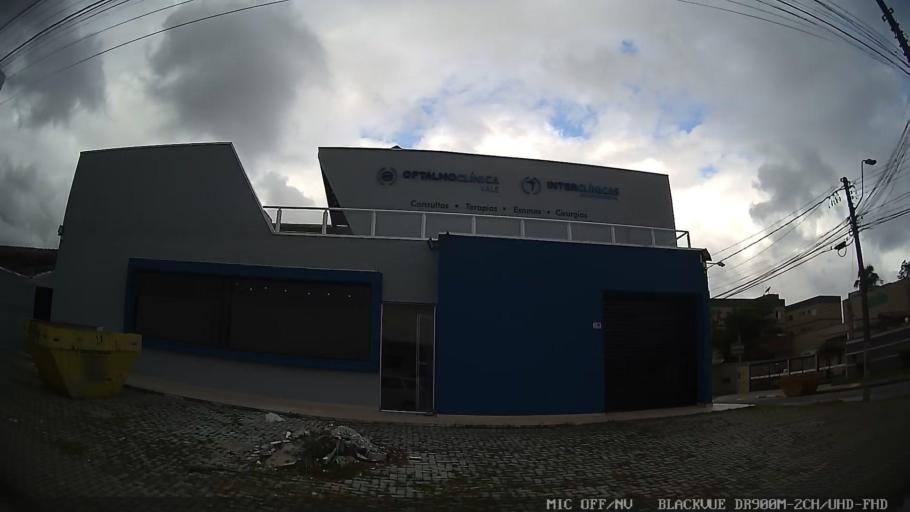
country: BR
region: Sao Paulo
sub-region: Caraguatatuba
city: Caraguatatuba
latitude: -23.6376
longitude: -45.4247
